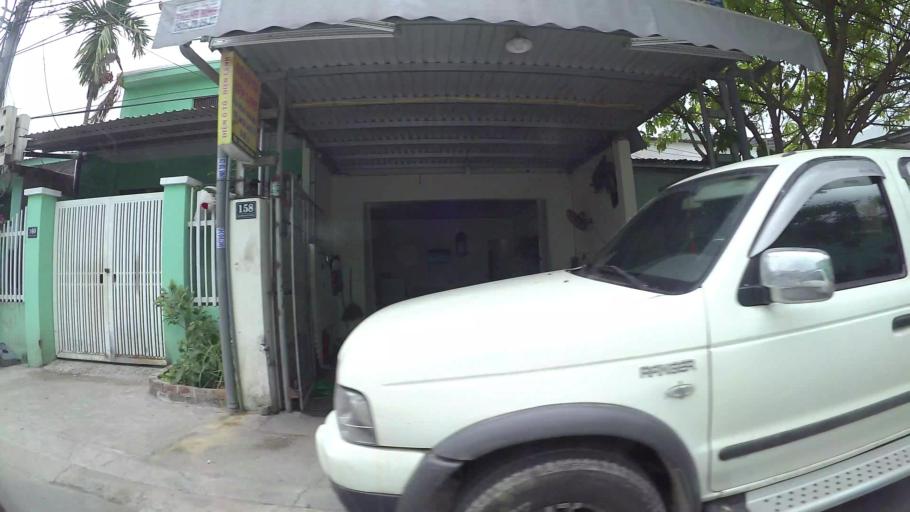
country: VN
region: Da Nang
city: Lien Chieu
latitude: 16.0481
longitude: 108.1699
